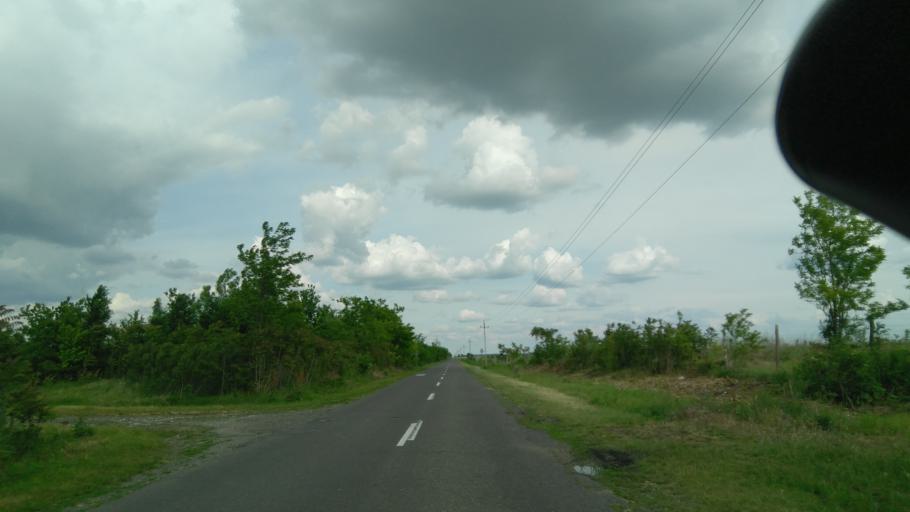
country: HU
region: Bekes
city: Mezohegyes
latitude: 46.3108
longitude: 20.8635
